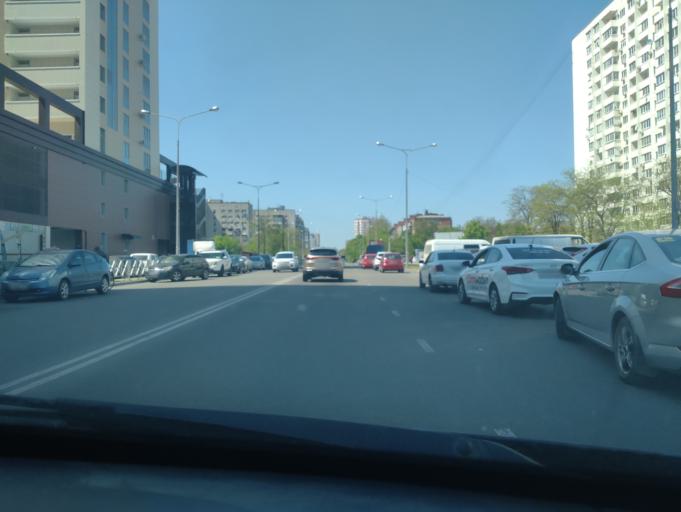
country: RU
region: Krasnodarskiy
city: Krasnodar
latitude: 45.0627
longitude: 39.0097
